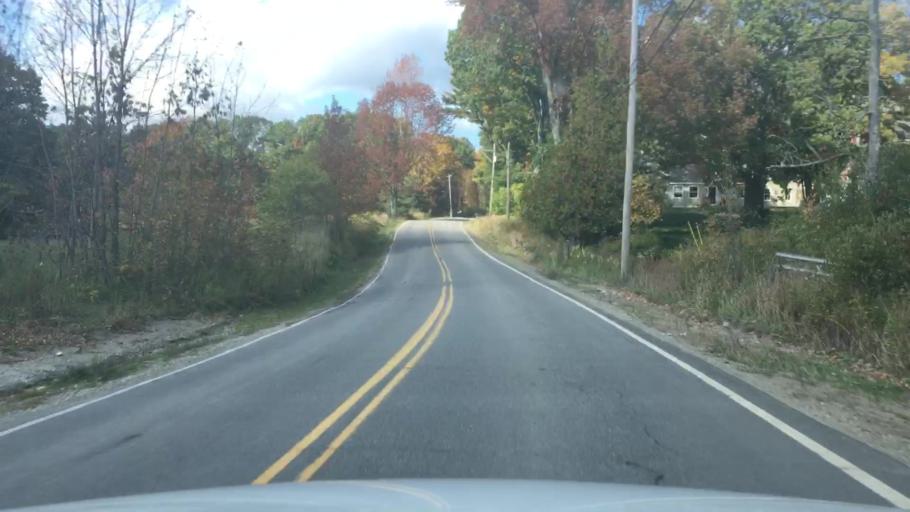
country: US
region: Maine
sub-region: Knox County
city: Warren
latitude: 44.1546
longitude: -69.2409
